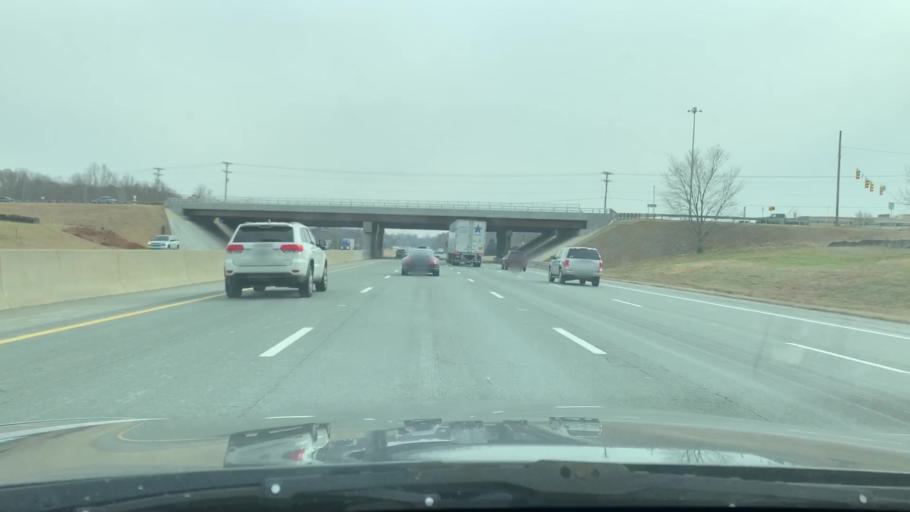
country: US
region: North Carolina
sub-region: Alamance County
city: Mebane
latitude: 36.0684
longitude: -79.3003
